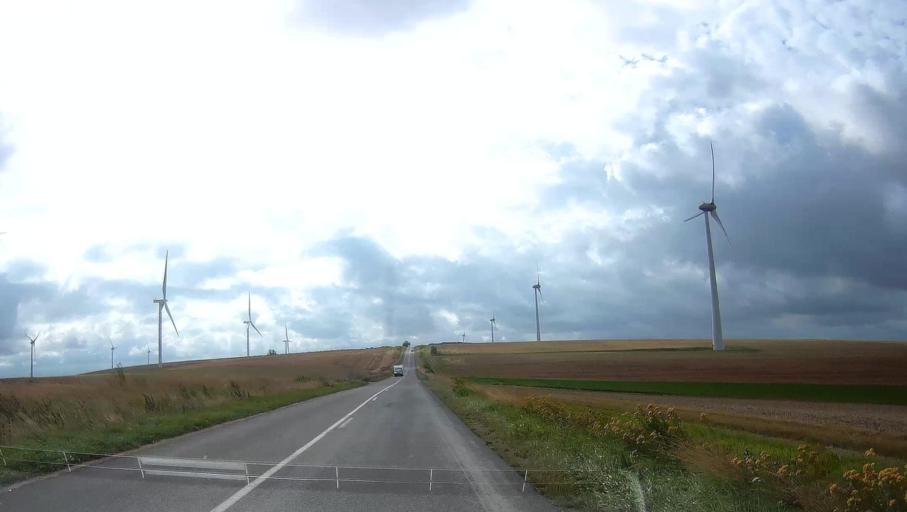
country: FR
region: Champagne-Ardenne
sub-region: Departement des Ardennes
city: Rethel
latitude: 49.5391
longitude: 4.3140
